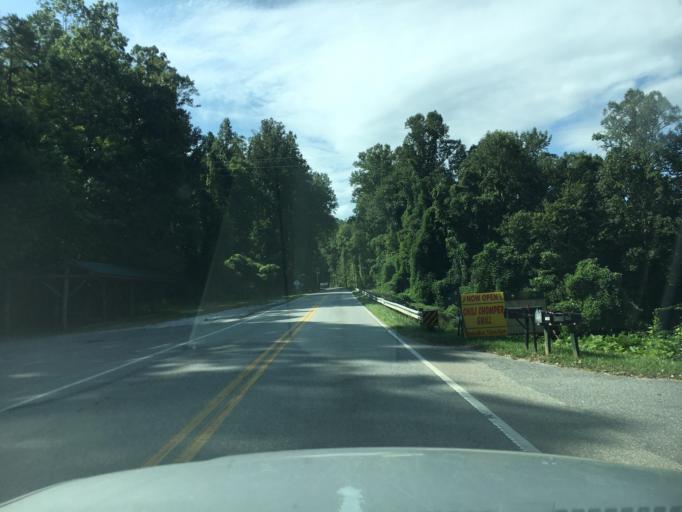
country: US
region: North Carolina
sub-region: Swain County
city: Bryson City
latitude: 35.3556
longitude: -83.5528
